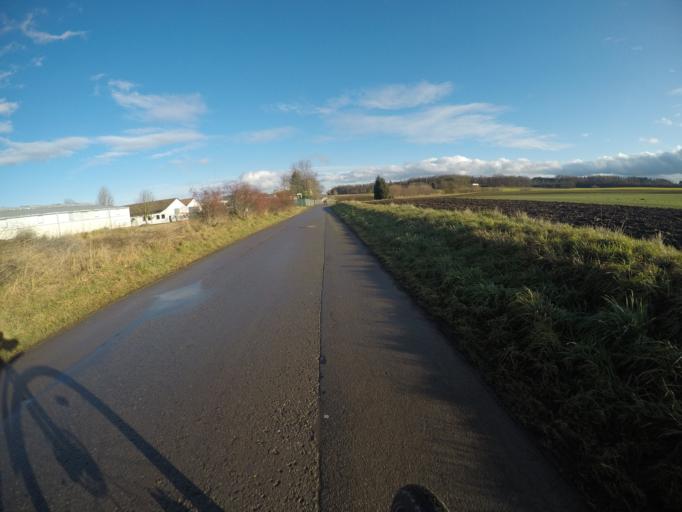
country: DE
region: Baden-Wuerttemberg
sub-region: Regierungsbezirk Stuttgart
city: Bondorf
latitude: 48.5272
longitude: 8.8766
